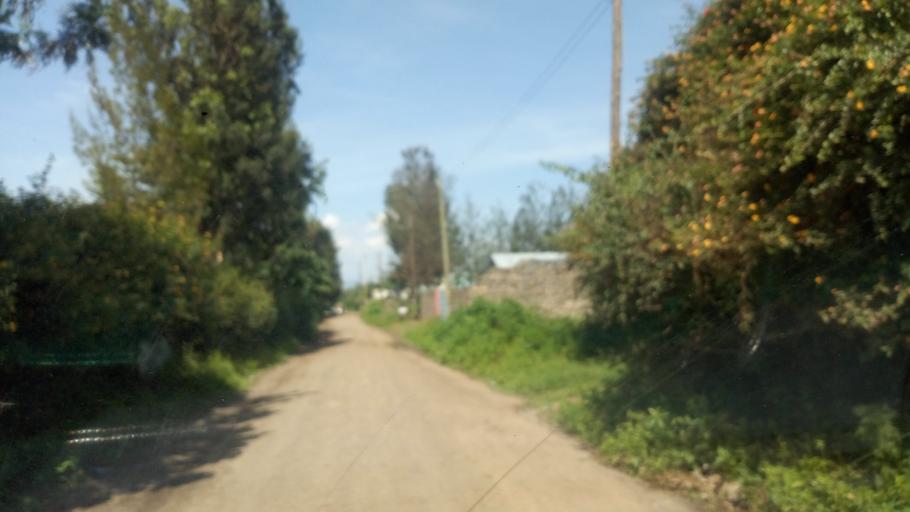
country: KE
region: Nakuru
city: Nakuru
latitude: -0.2761
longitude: 36.1128
